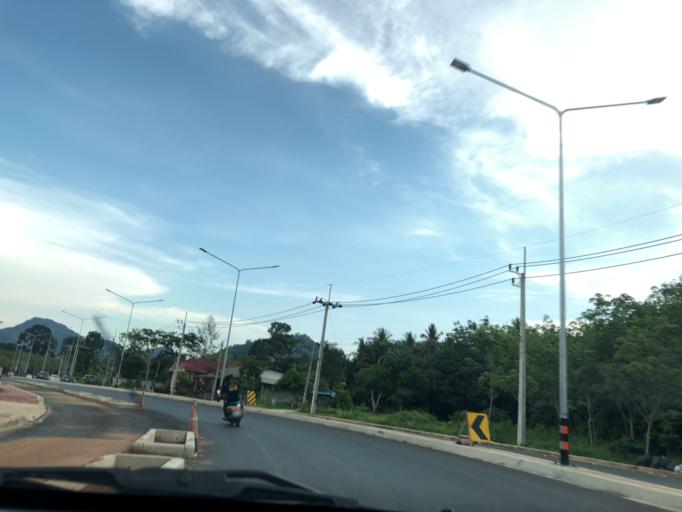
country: TH
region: Phangnga
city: Ban Ao Nang
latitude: 8.0606
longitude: 98.8406
